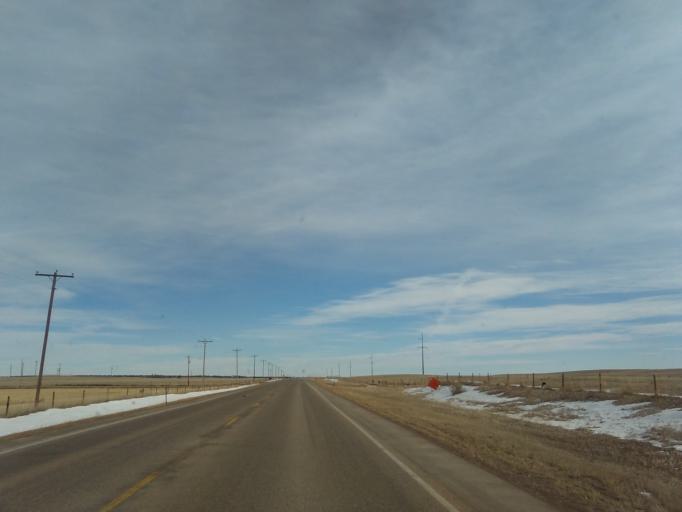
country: US
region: Wyoming
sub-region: Laramie County
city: Ranchettes
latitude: 41.4084
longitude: -104.4424
